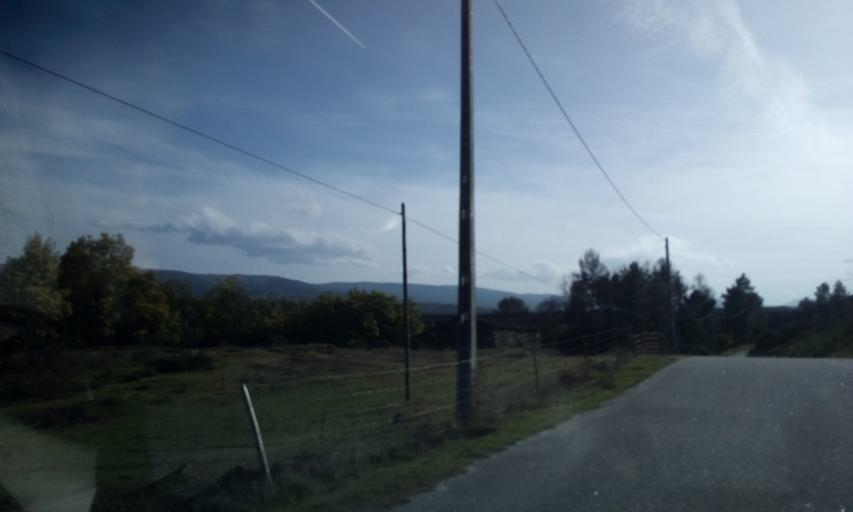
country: PT
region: Guarda
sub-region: Celorico da Beira
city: Celorico da Beira
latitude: 40.6348
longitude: -7.4336
